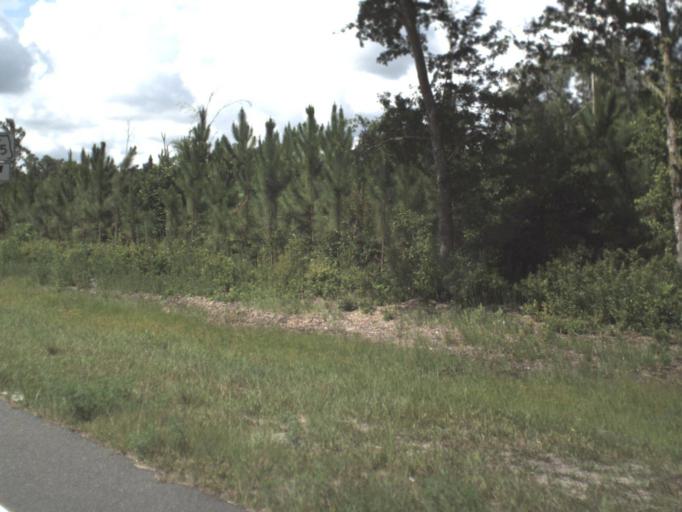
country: US
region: Florida
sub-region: Alachua County
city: Alachua
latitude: 29.8435
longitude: -82.3472
